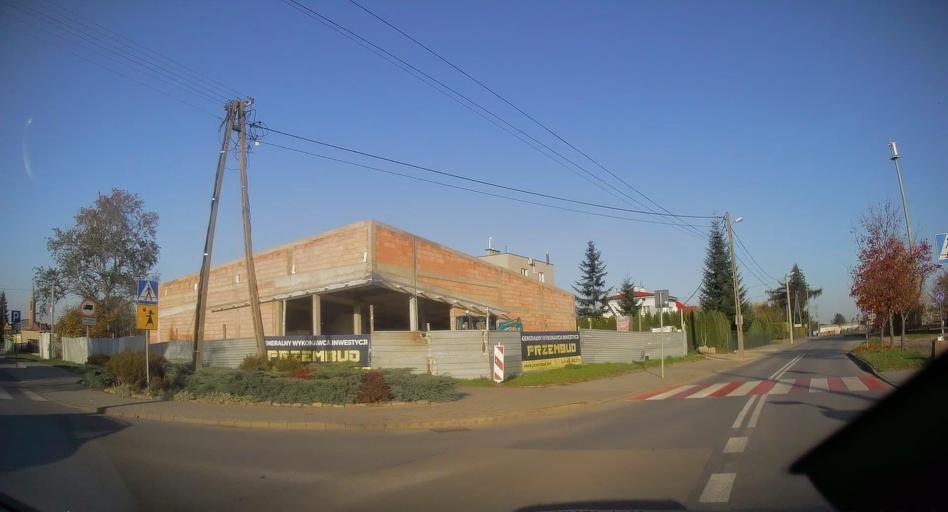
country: PL
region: Subcarpathian Voivodeship
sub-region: Powiat debicki
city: Debica
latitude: 50.0553
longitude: 21.4049
